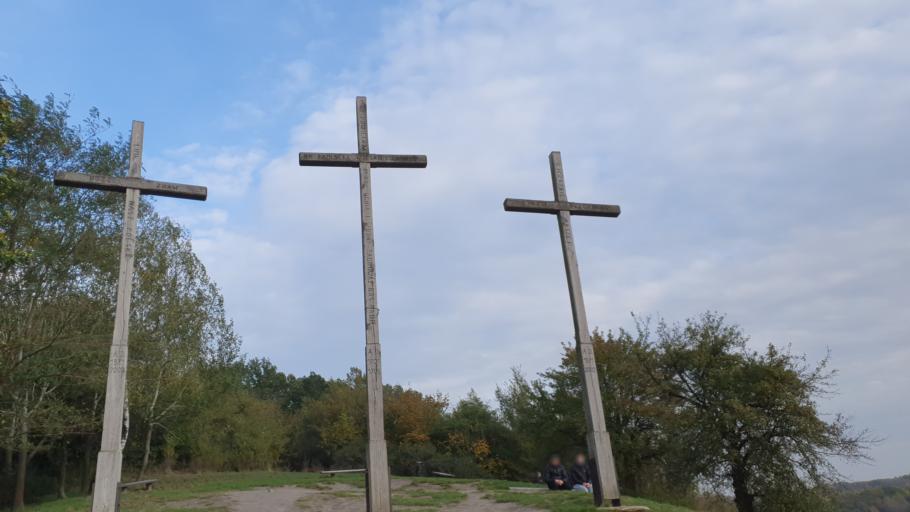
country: PL
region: Lublin Voivodeship
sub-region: Powiat pulawski
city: Kazimierz Dolny
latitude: 51.3219
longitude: 21.9505
